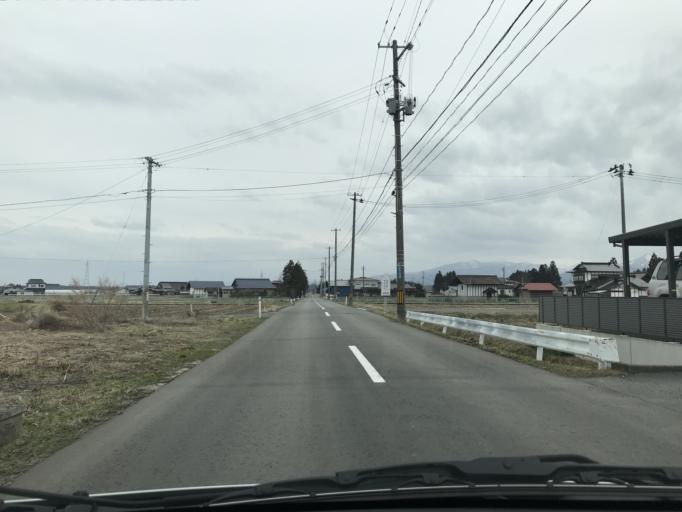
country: JP
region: Iwate
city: Kitakami
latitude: 39.3115
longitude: 141.0591
